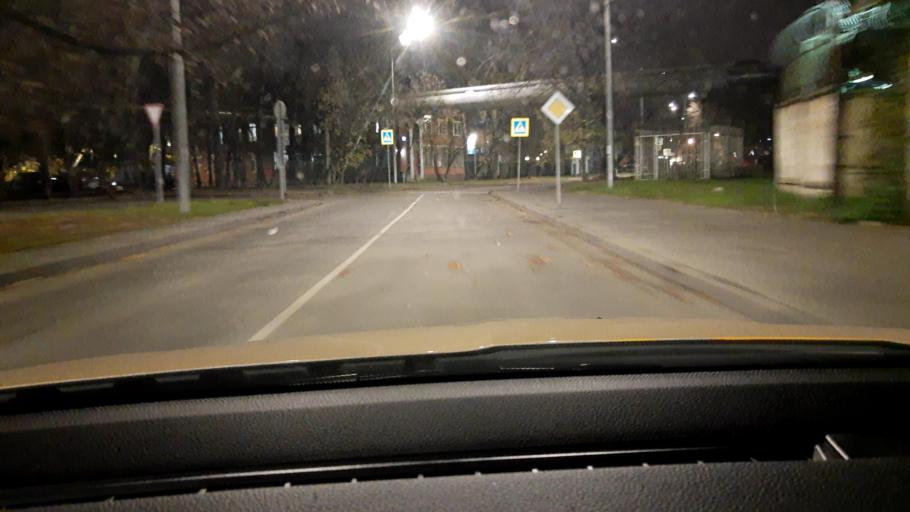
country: RU
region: Moscow
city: Lefortovo
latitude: 55.7506
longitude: 37.7248
